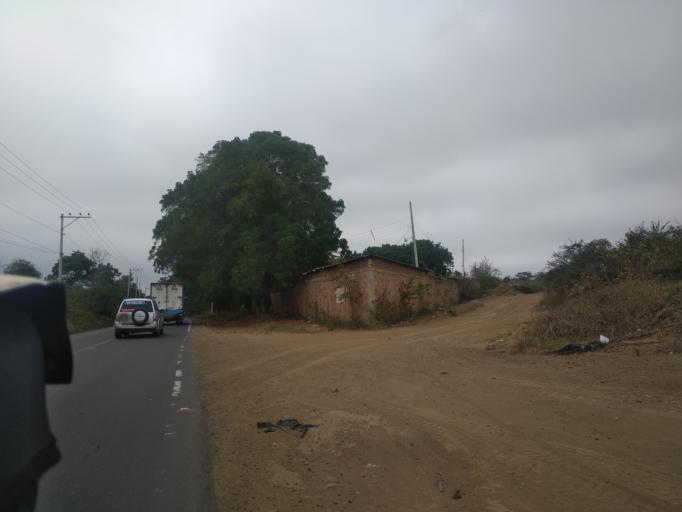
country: EC
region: Manabi
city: Montecristi
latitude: -1.0700
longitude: -80.6613
